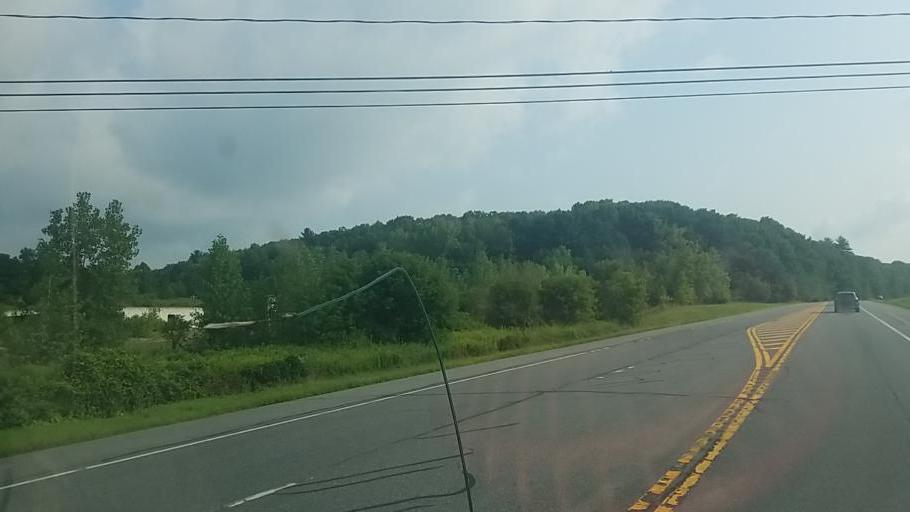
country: US
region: New York
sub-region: Fulton County
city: Gloversville
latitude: 43.0351
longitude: -74.3424
